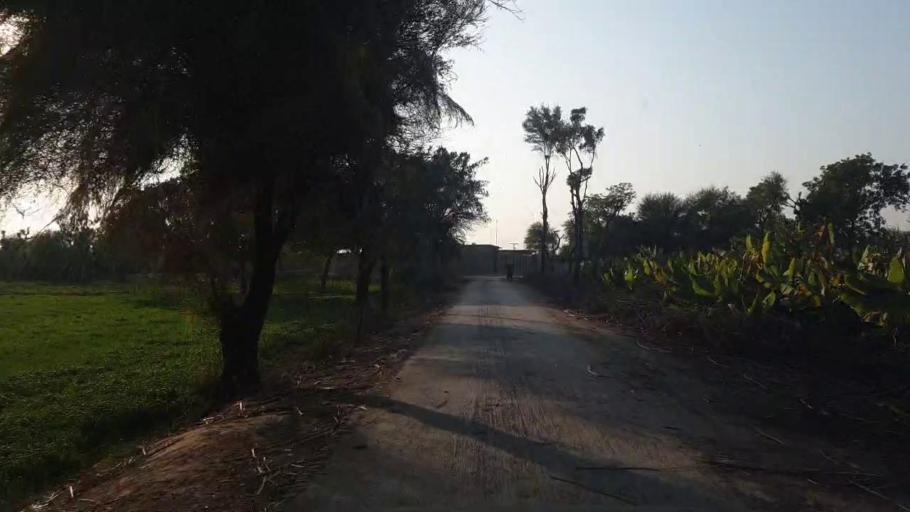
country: PK
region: Sindh
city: Shahdadpur
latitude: 25.8827
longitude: 68.5819
